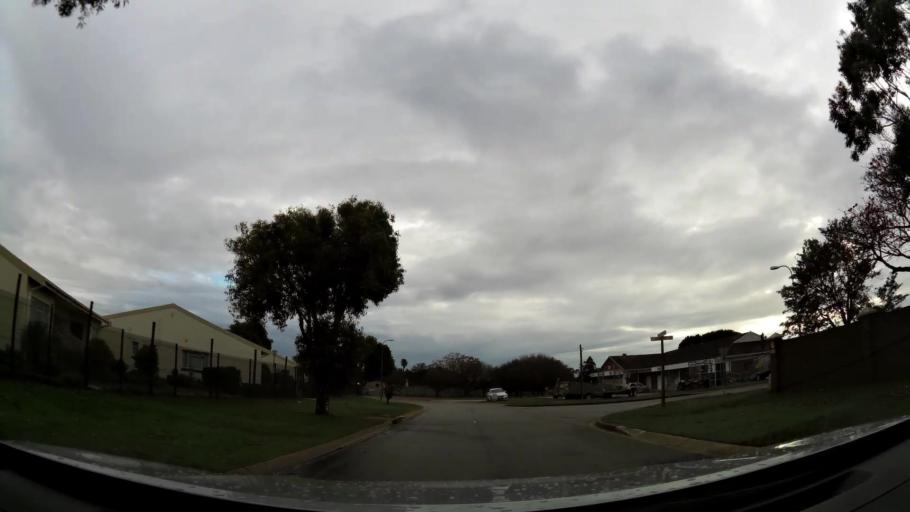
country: ZA
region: Eastern Cape
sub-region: Nelson Mandela Bay Metropolitan Municipality
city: Port Elizabeth
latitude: -33.9848
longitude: 25.5643
